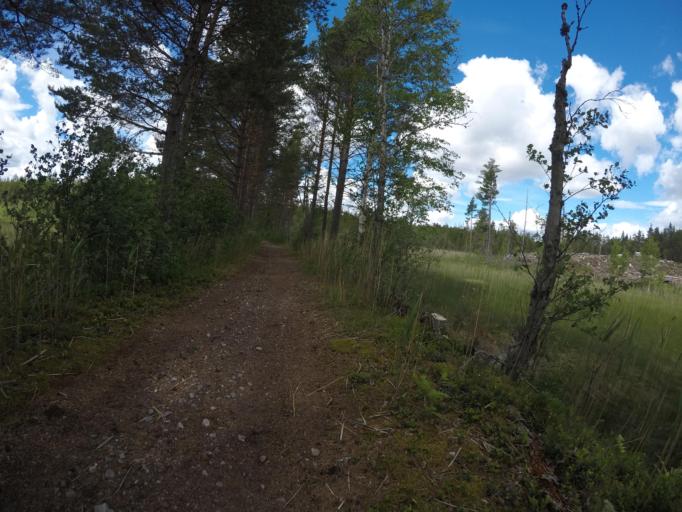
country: SE
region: Vaermland
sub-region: Filipstads Kommun
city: Lesjofors
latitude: 60.1390
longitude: 14.2954
